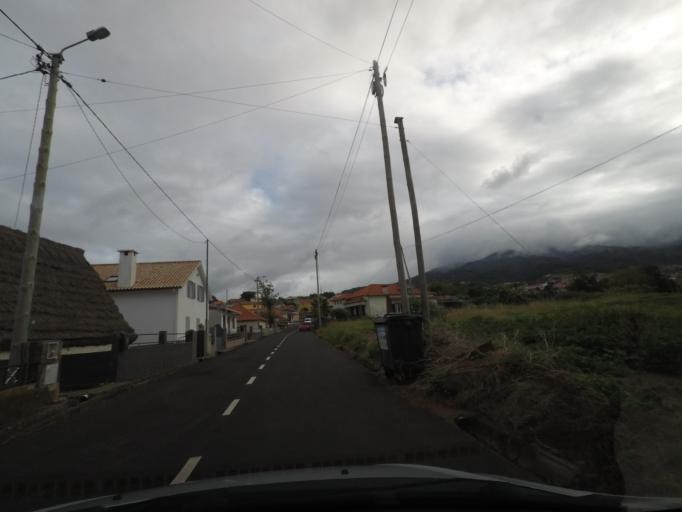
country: PT
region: Madeira
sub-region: Santana
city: Santana
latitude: 32.8094
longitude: -16.8767
